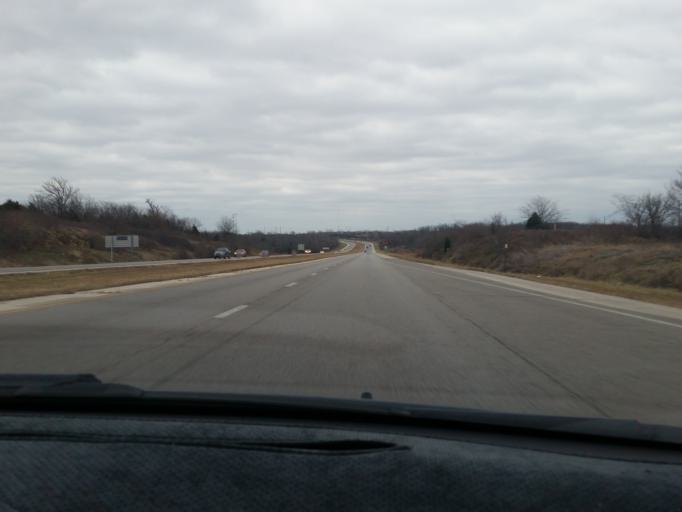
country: US
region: Kansas
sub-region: Johnson County
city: Olathe
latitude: 38.9464
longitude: -94.8809
